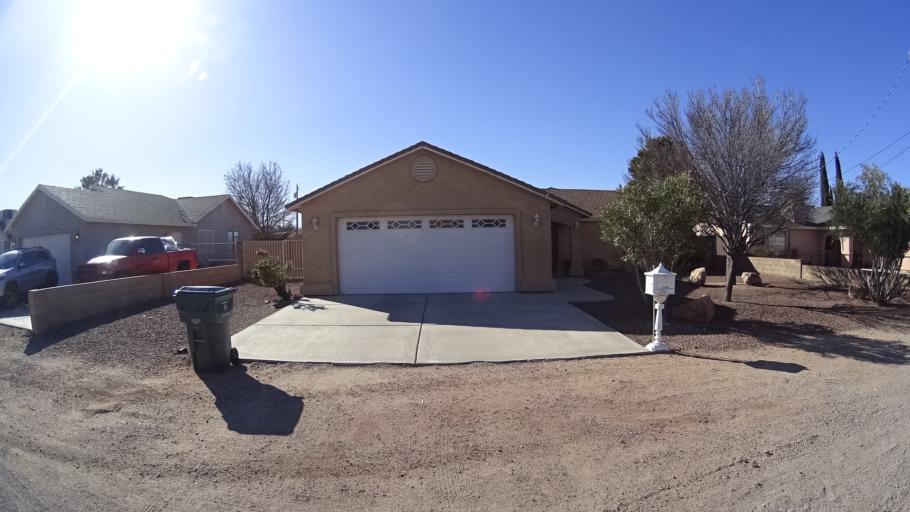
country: US
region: Arizona
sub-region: Mohave County
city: Kingman
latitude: 35.2055
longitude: -114.0144
